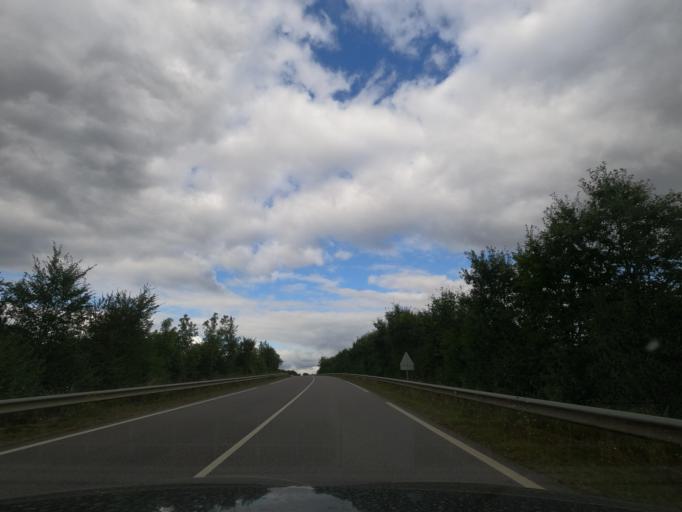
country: FR
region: Lower Normandy
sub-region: Departement de l'Orne
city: Gace
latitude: 48.8717
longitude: 0.3793
